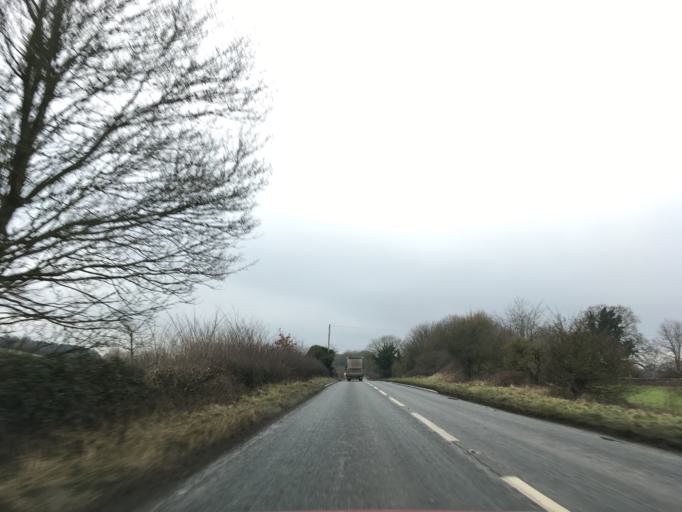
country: GB
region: England
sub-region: Gloucestershire
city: Tetbury
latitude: 51.6539
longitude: -2.1312
